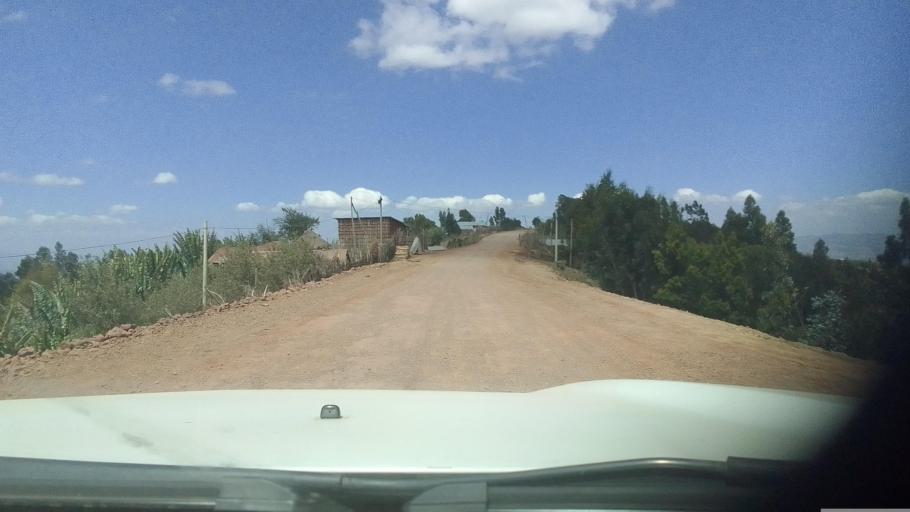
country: ET
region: Oromiya
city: Hagere Hiywet
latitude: 8.8384
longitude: 37.8861
